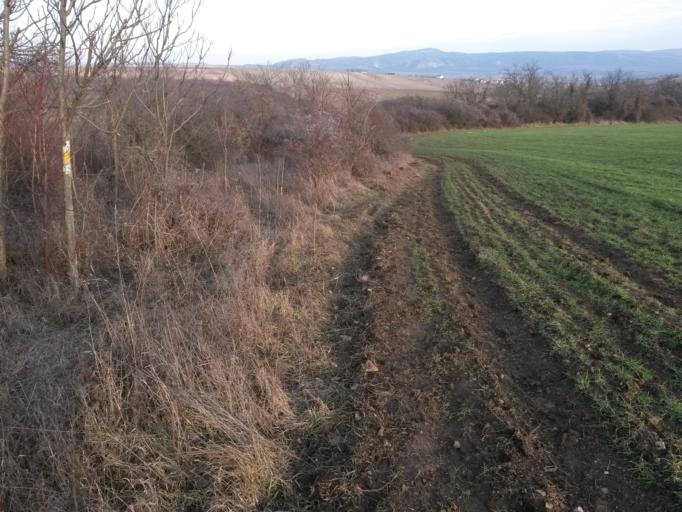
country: HU
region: Pest
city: Perbal
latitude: 47.5951
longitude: 18.7330
